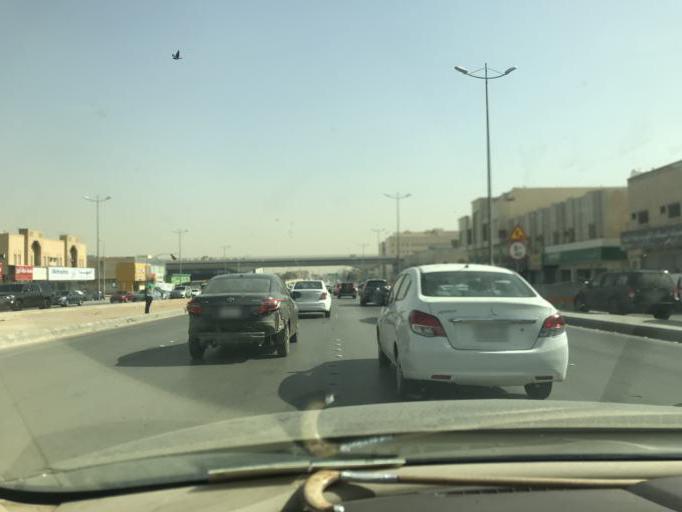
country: SA
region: Ar Riyad
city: Riyadh
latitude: 24.7949
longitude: 46.7428
